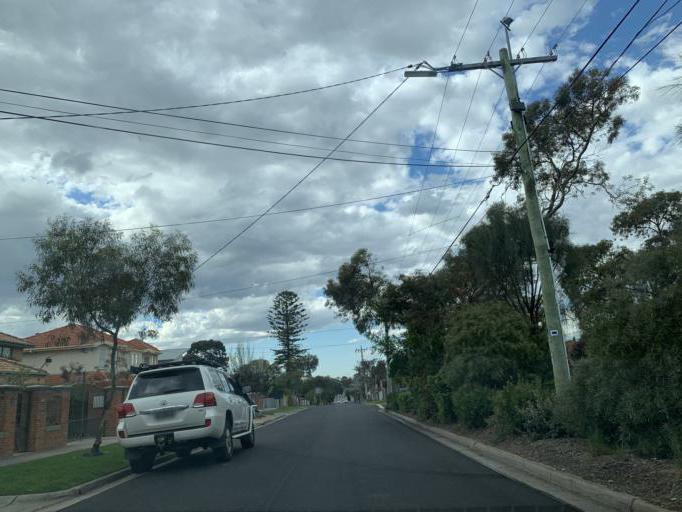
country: AU
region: Victoria
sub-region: Bayside
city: Hampton East
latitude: -37.9337
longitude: 145.0202
